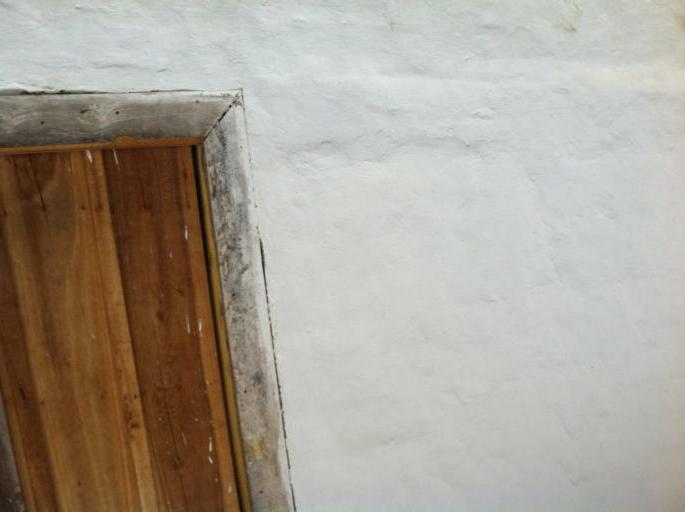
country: CO
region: Quindio
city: Genova
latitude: 4.2086
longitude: -75.7902
